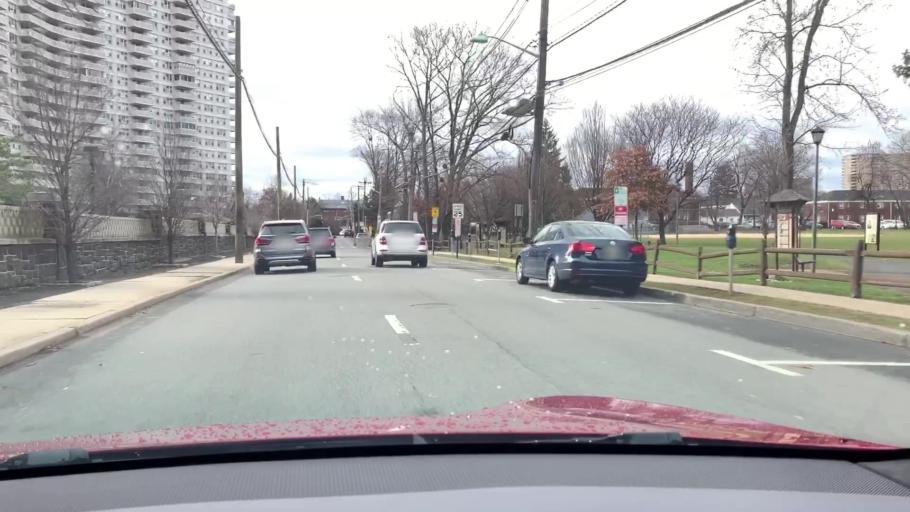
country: US
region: New Jersey
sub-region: Bergen County
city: Fort Lee
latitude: 40.8554
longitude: -73.9733
